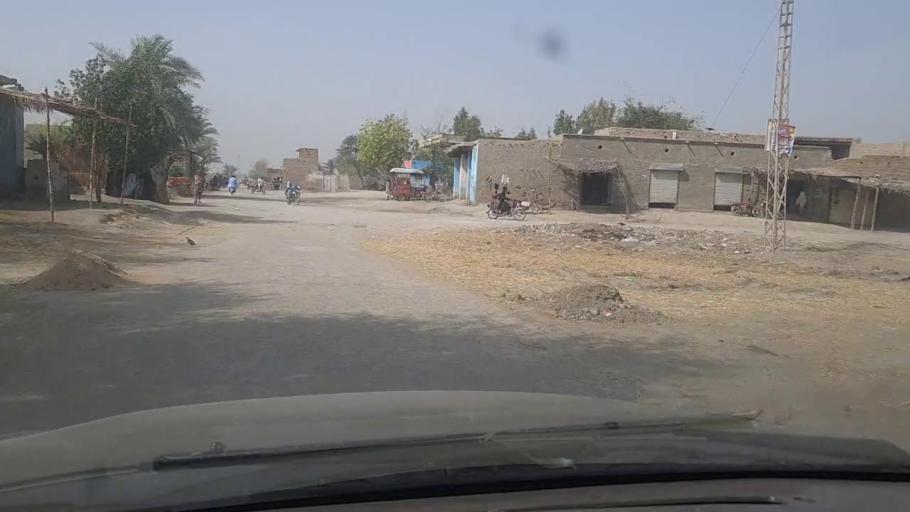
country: PK
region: Sindh
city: Garhi Yasin
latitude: 27.8704
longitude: 68.5577
